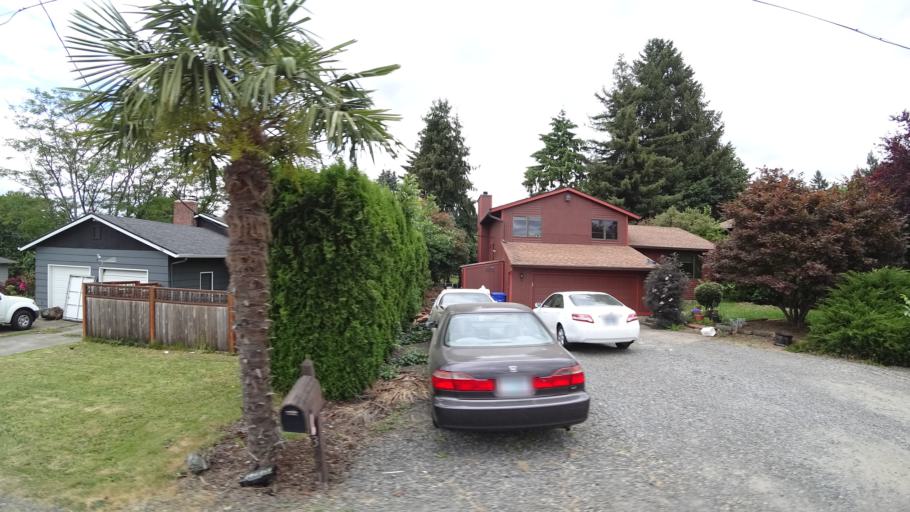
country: US
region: Oregon
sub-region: Clackamas County
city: Happy Valley
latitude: 45.4863
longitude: -122.5209
